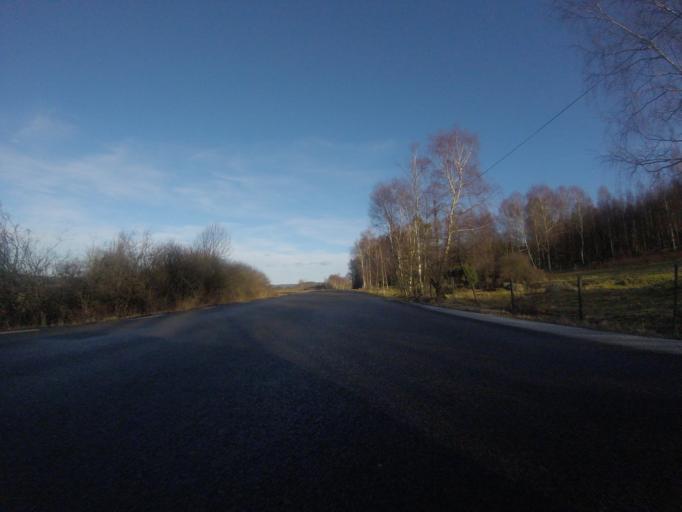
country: SE
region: Halland
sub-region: Varbergs Kommun
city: Veddige
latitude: 57.2270
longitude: 12.2603
